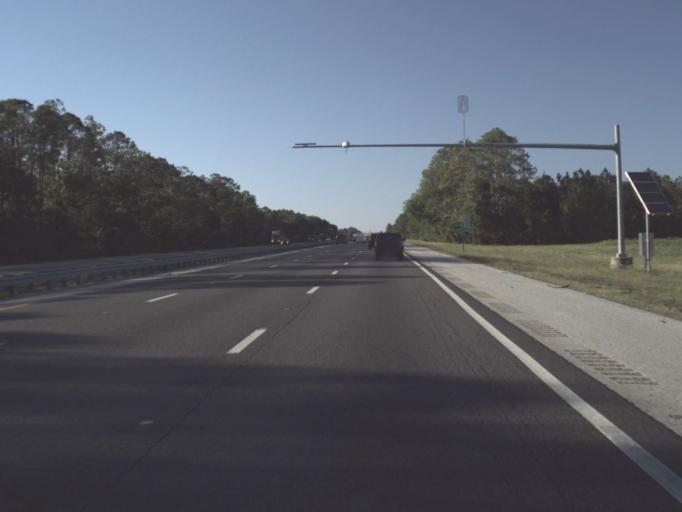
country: US
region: Florida
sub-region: Flagler County
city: Flagler Beach
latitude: 29.4849
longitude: -81.1870
